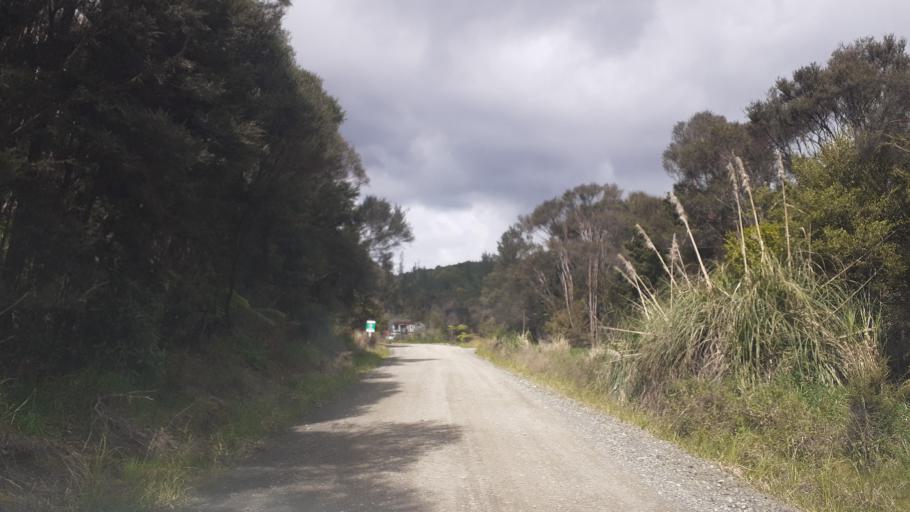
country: NZ
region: Northland
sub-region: Far North District
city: Moerewa
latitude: -35.5833
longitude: 173.9395
